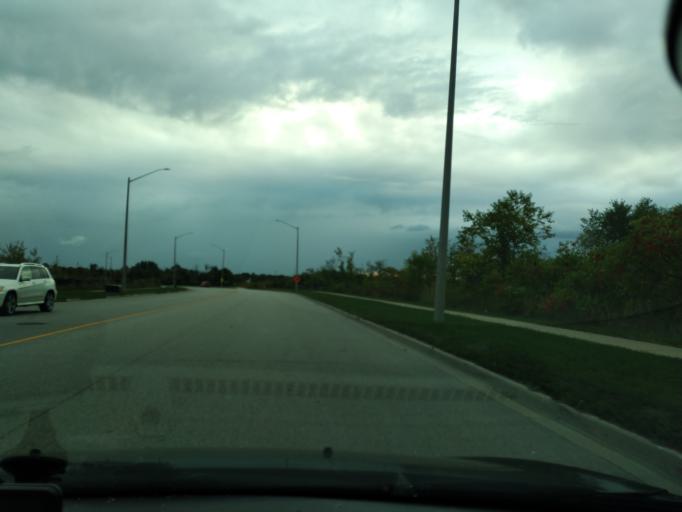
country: CA
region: Ontario
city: Innisfil
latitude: 44.3028
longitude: -79.5592
